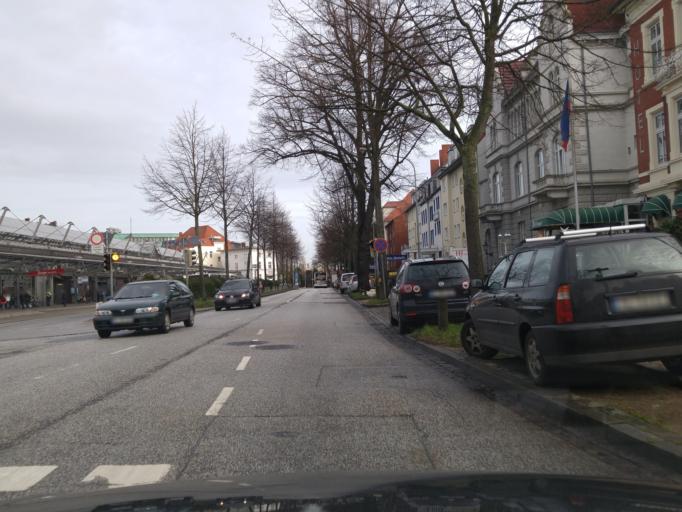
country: DE
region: Schleswig-Holstein
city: Luebeck
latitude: 53.8650
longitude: 10.6703
